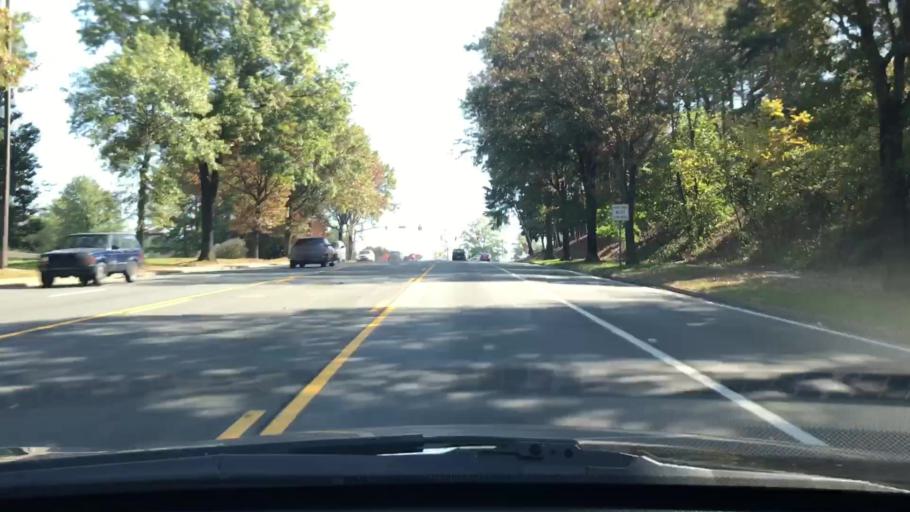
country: US
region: Georgia
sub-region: Gwinnett County
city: Norcross
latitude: 33.9200
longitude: -84.1996
